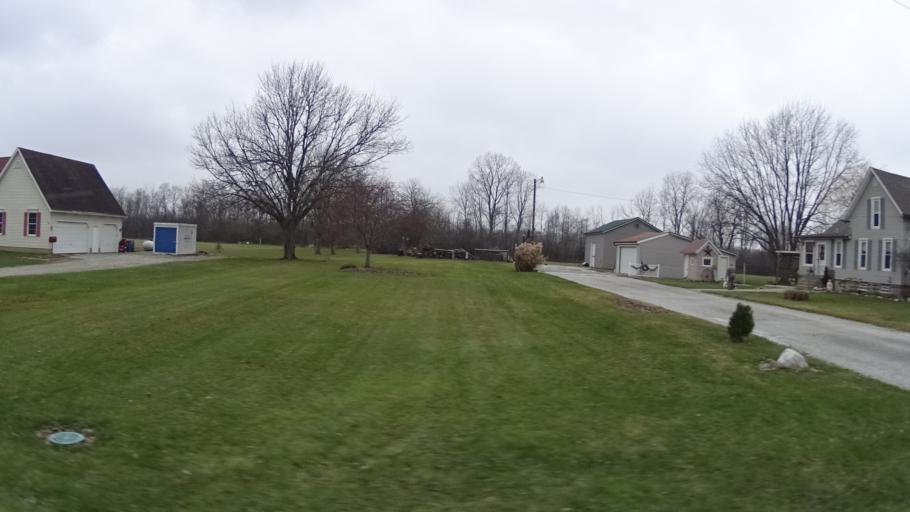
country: US
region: Ohio
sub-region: Lorain County
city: Oberlin
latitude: 41.3031
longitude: -82.2380
